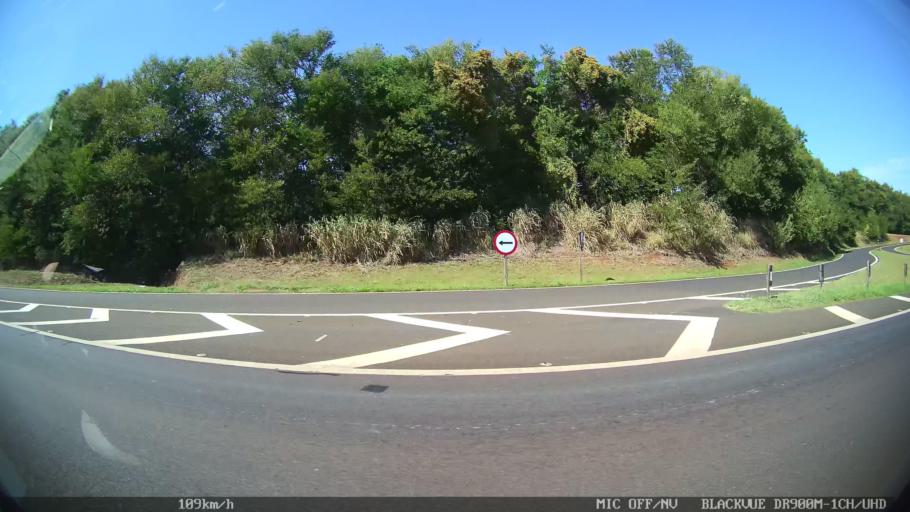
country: BR
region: Sao Paulo
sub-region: Franca
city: Franca
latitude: -20.5896
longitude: -47.4372
